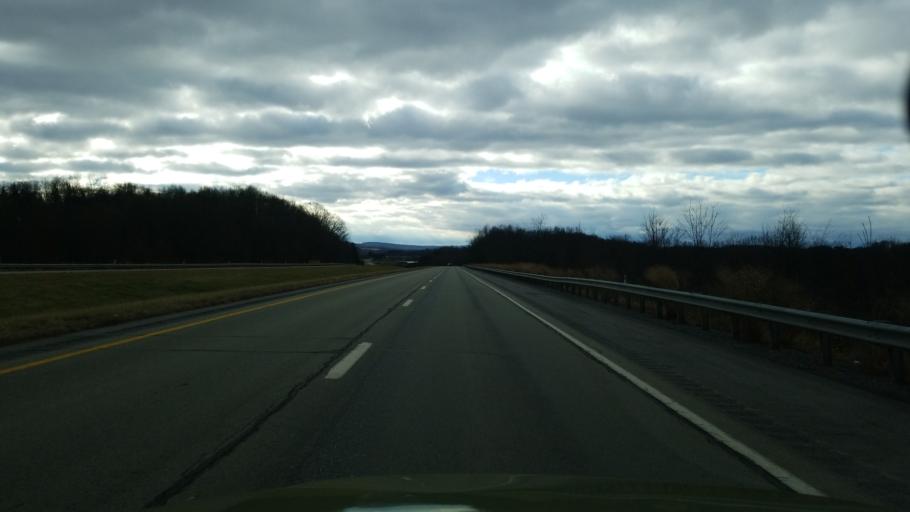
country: US
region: Pennsylvania
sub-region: Indiana County
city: Chevy Chase Heights
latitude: 40.6456
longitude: -79.1173
